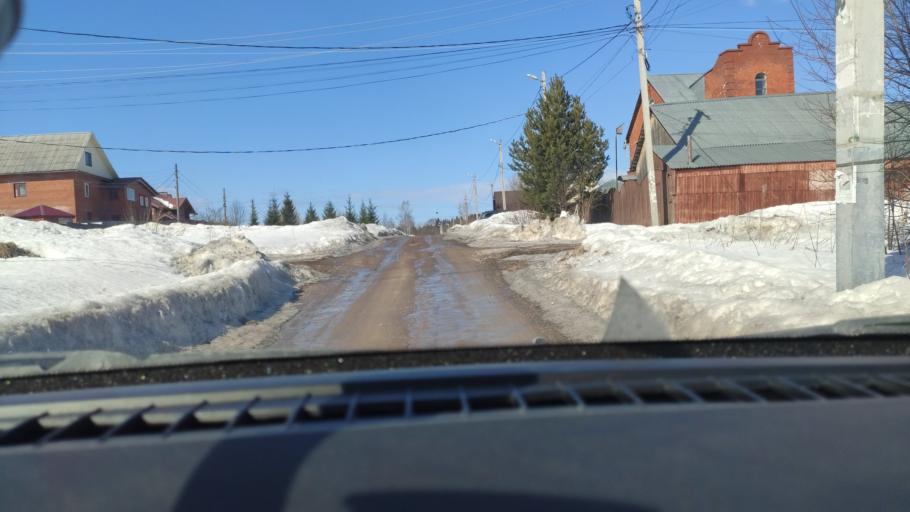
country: RU
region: Perm
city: Perm
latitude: 58.0372
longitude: 56.3956
